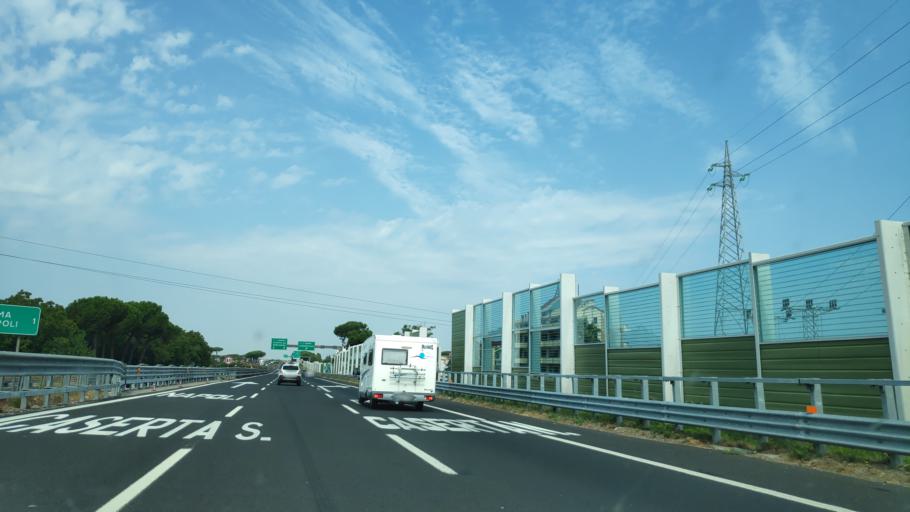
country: IT
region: Campania
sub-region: Provincia di Caserta
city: San Marco Evangelista
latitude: 41.0339
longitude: 14.3344
